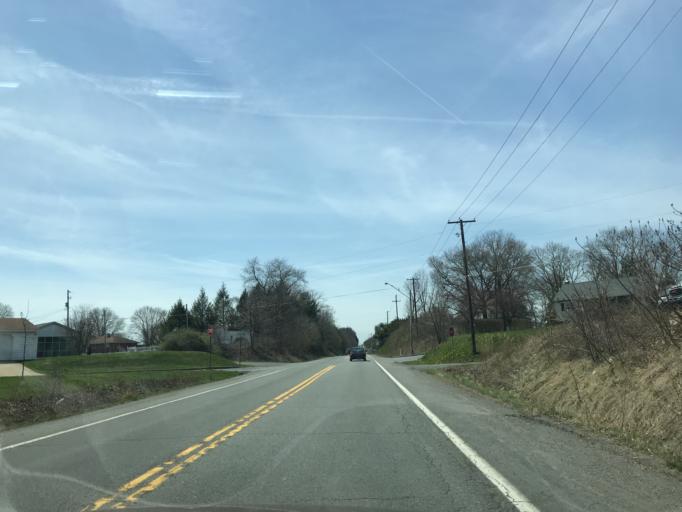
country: US
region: Pennsylvania
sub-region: Snyder County
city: Selinsgrove
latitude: 40.8113
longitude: -76.8598
